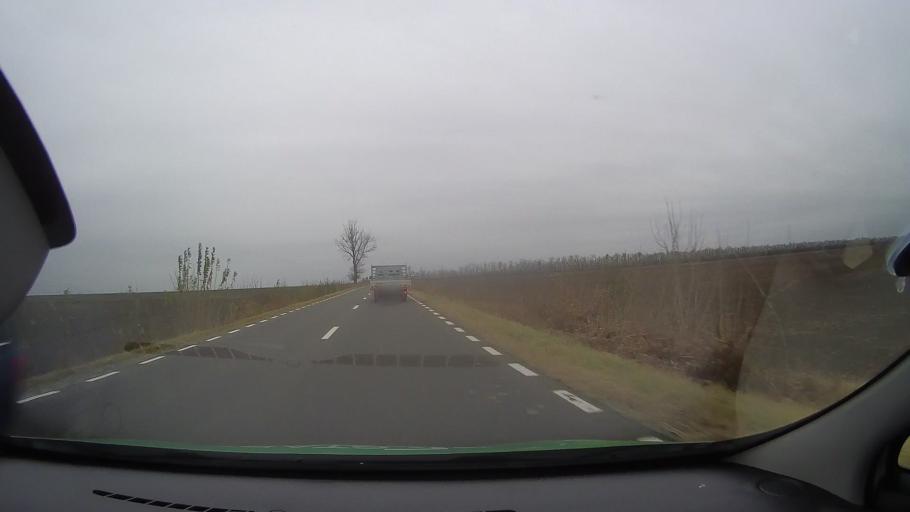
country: RO
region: Ialomita
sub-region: Comuna Gheorghe Lazar
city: Gheorghe Lazar
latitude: 44.6760
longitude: 27.4185
